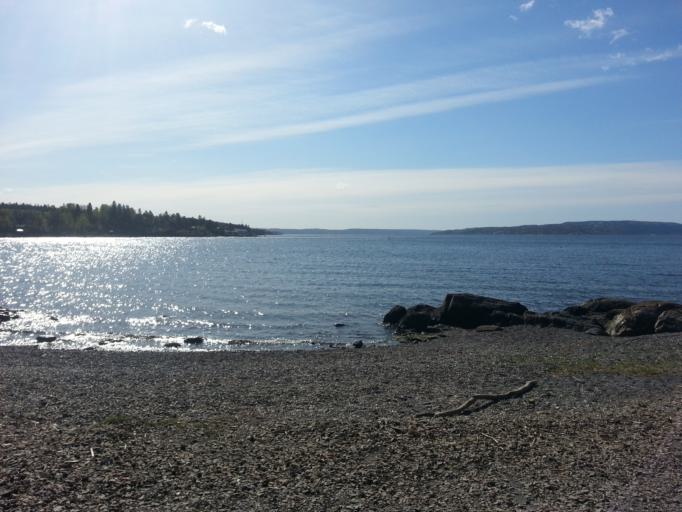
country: NO
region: Akershus
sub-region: Baerum
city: Lysaker
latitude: 59.9123
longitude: 10.6501
